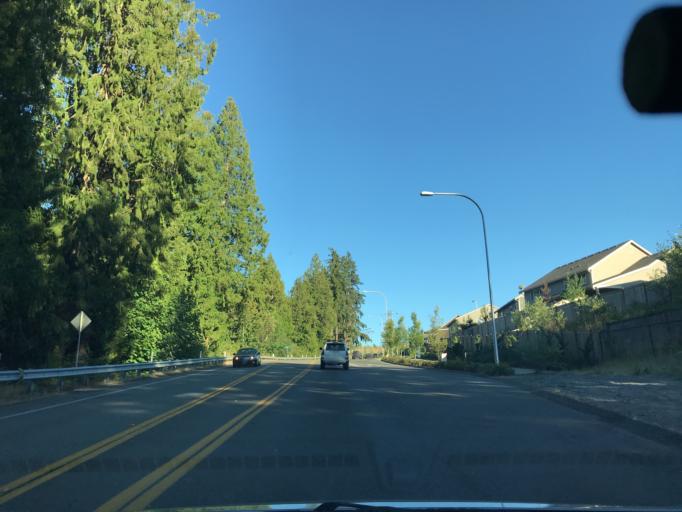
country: US
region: Washington
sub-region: King County
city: Pacific
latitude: 47.2651
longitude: -122.2010
